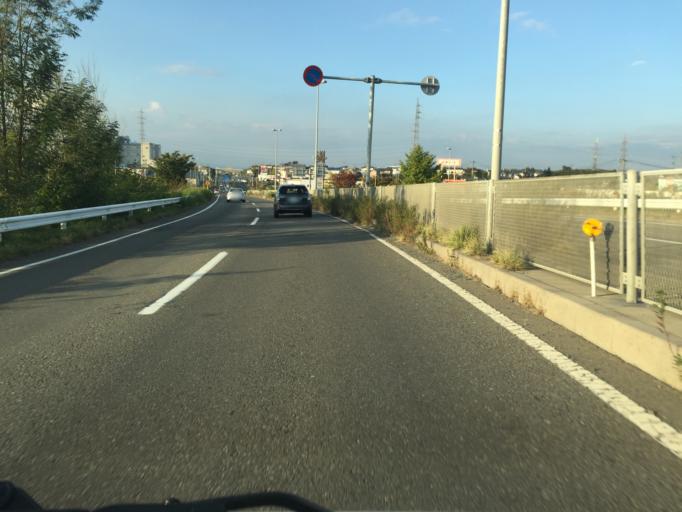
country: JP
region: Fukushima
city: Koriyama
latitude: 37.4451
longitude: 140.3793
